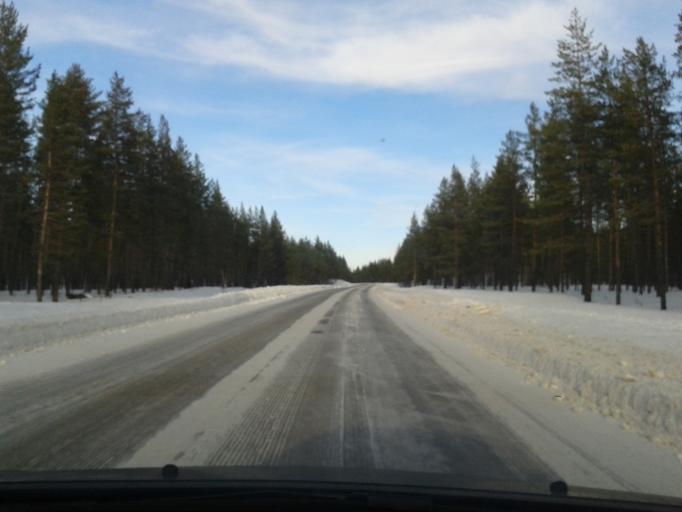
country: SE
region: Vaesternorrland
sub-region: OErnskoeldsviks Kommun
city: Bredbyn
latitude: 63.6121
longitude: 17.9022
